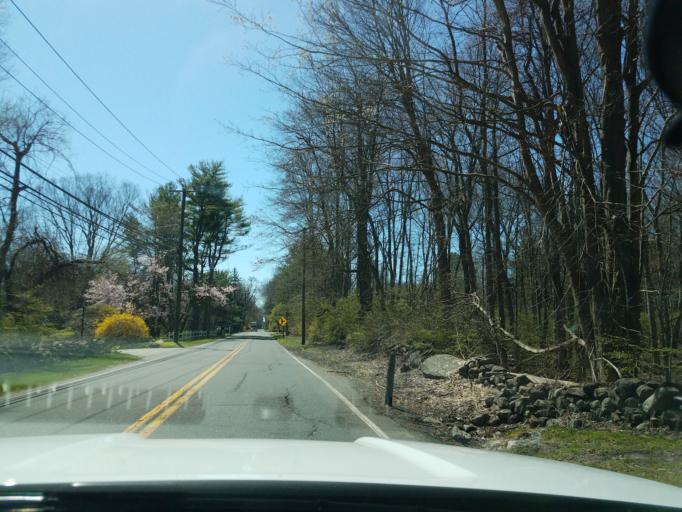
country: US
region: Connecticut
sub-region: Fairfield County
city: Westport
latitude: 41.2068
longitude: -73.3705
